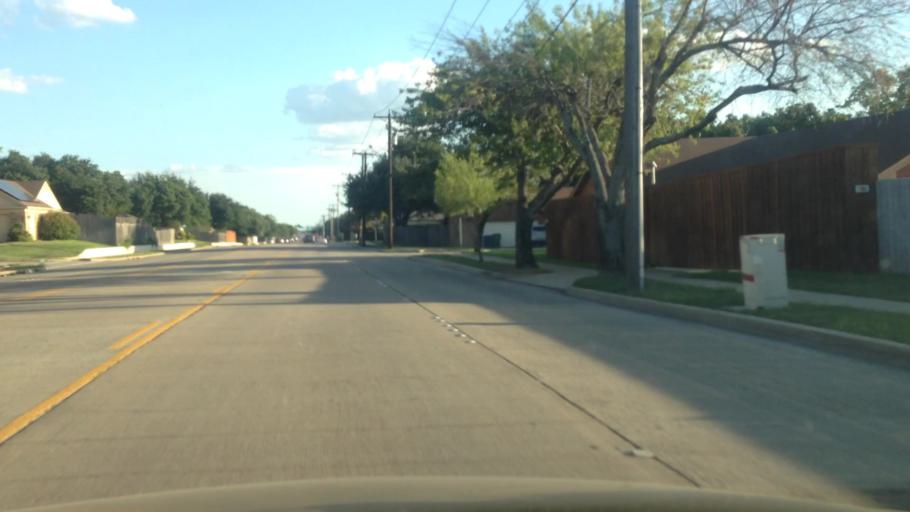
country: US
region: Texas
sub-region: Tarrant County
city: Watauga
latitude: 32.8852
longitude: -97.2379
